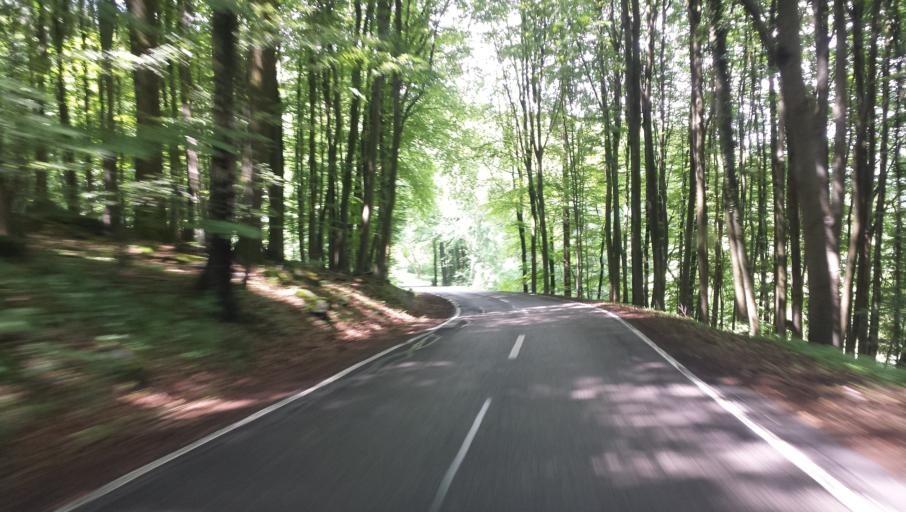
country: DE
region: Hesse
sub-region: Regierungsbezirk Darmstadt
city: Lindenfels
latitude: 49.6901
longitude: 8.7481
